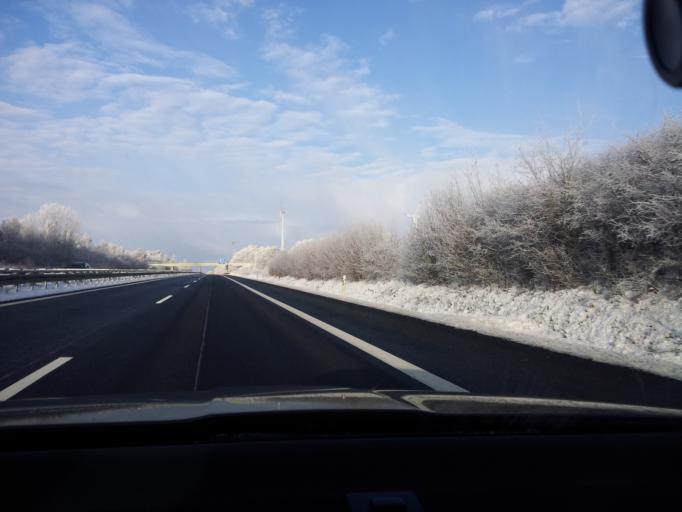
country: DE
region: Brandenburg
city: Gerdshagen
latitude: 53.2217
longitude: 12.2305
